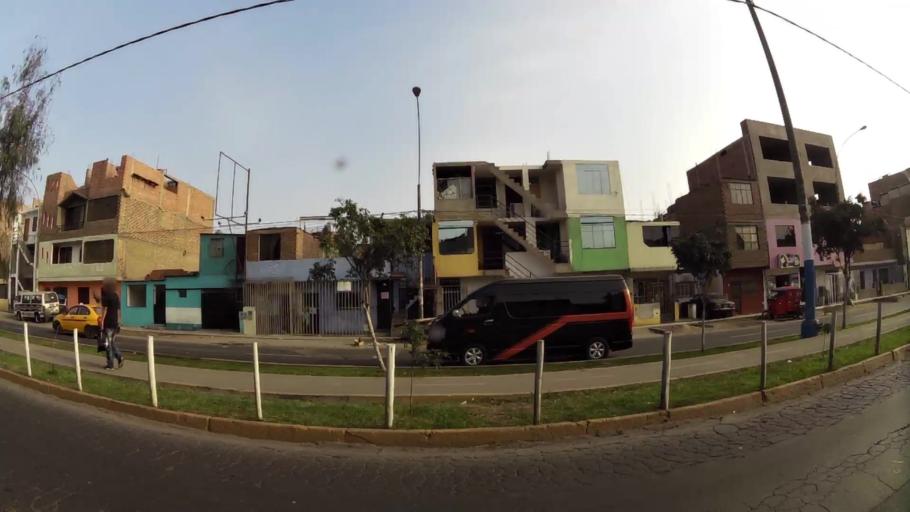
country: PE
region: Lima
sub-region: Lima
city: Independencia
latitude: -12.0249
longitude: -77.0784
